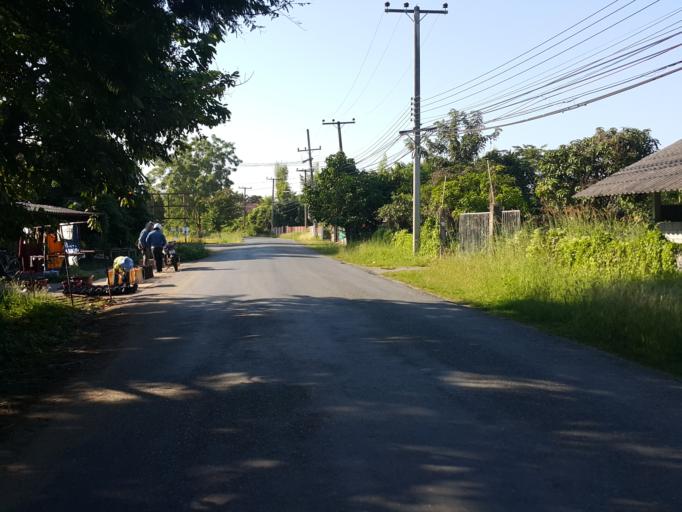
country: TH
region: Chiang Mai
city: San Kamphaeng
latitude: 18.8105
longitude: 99.1376
